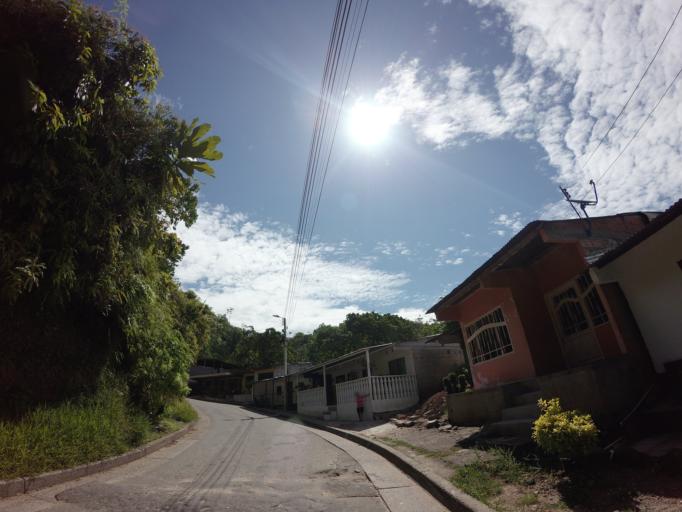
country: CO
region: Caldas
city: Norcasia
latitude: 5.5734
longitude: -74.8933
